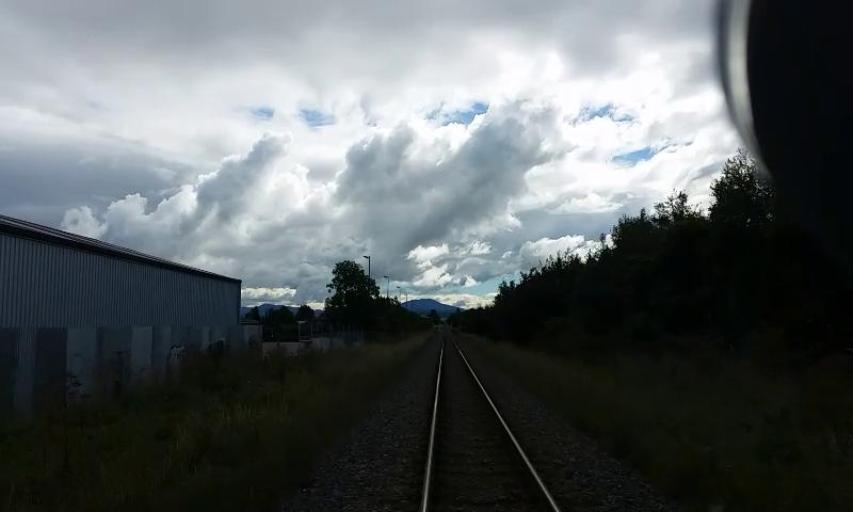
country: NZ
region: Canterbury
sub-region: Waimakariri District
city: Woodend
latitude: -43.3133
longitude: 172.6008
